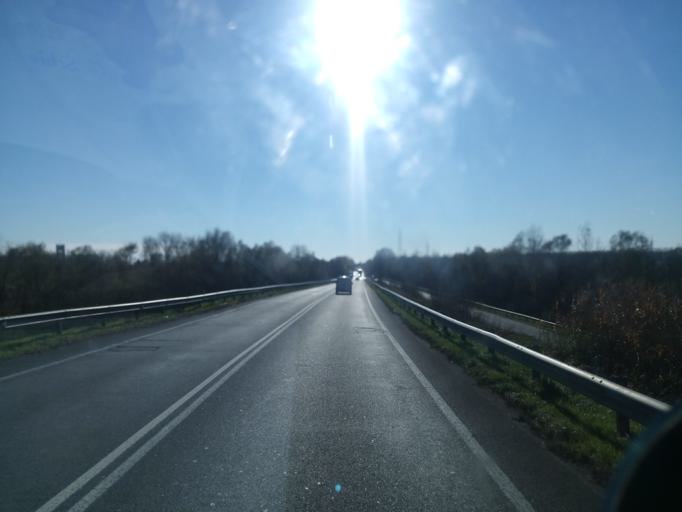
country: IT
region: Veneto
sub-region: Provincia di Padova
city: Mejaniga
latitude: 45.4653
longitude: 11.9211
